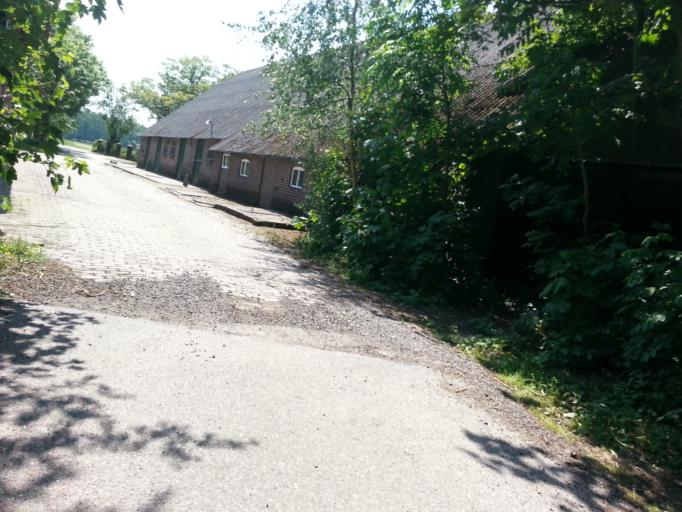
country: NL
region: Gelderland
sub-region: Gemeente Barneveld
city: Terschuur
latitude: 52.1141
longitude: 5.5226
